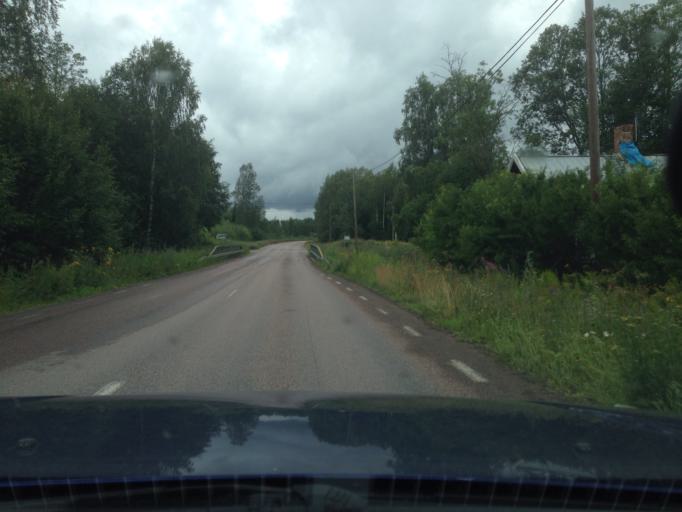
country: SE
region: Dalarna
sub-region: Ludvika Kommun
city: Ludvika
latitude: 60.1447
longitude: 15.1107
